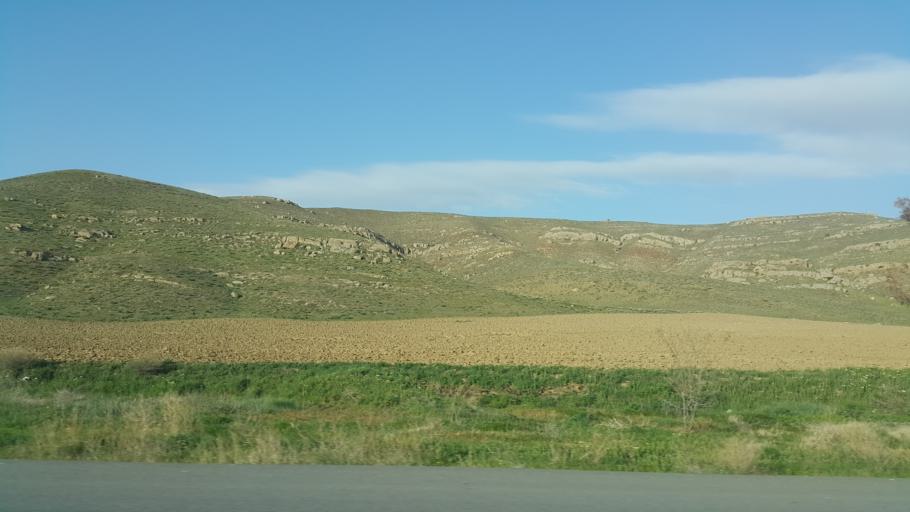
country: TR
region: Ankara
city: Sereflikochisar
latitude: 39.0933
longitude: 33.3918
